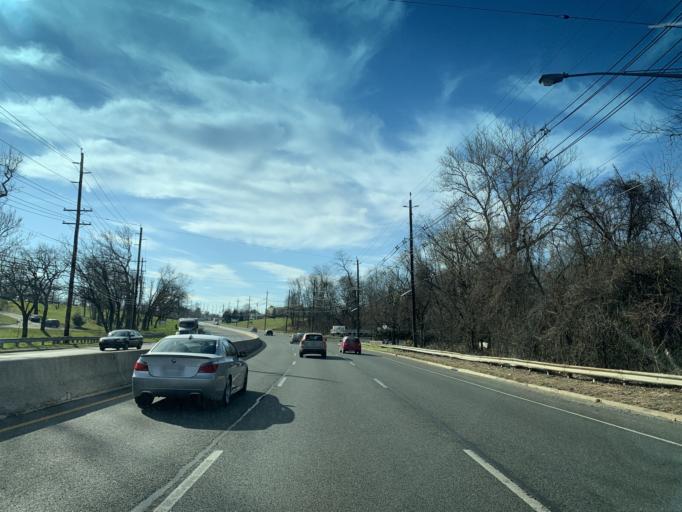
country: US
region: New Jersey
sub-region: Burlington County
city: Cinnaminson
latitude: 40.0038
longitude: -74.9821
